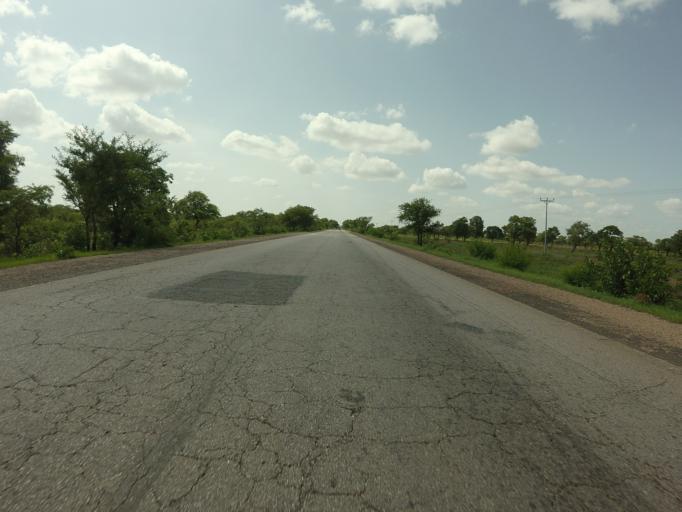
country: GH
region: Northern
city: Savelugu
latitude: 9.8259
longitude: -0.8641
